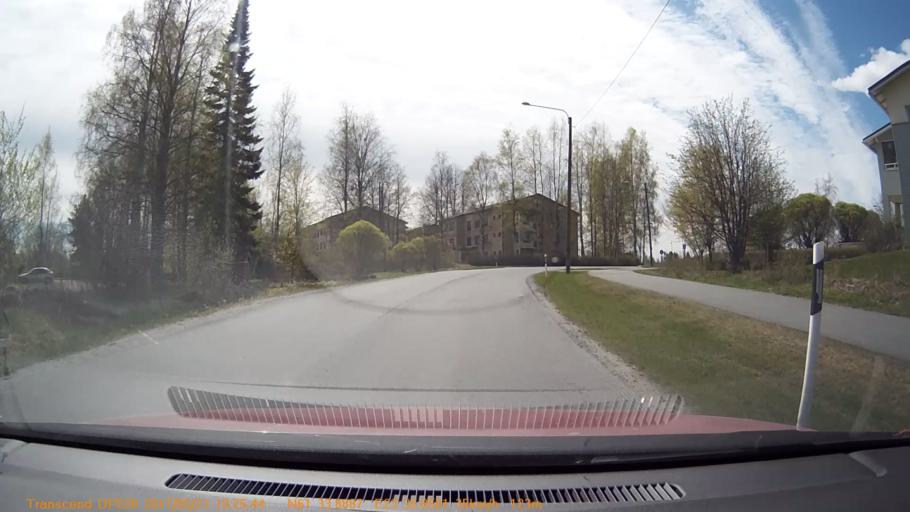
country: FI
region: Pirkanmaa
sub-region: Tampere
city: Yloejaervi
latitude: 61.5649
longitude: 23.5978
